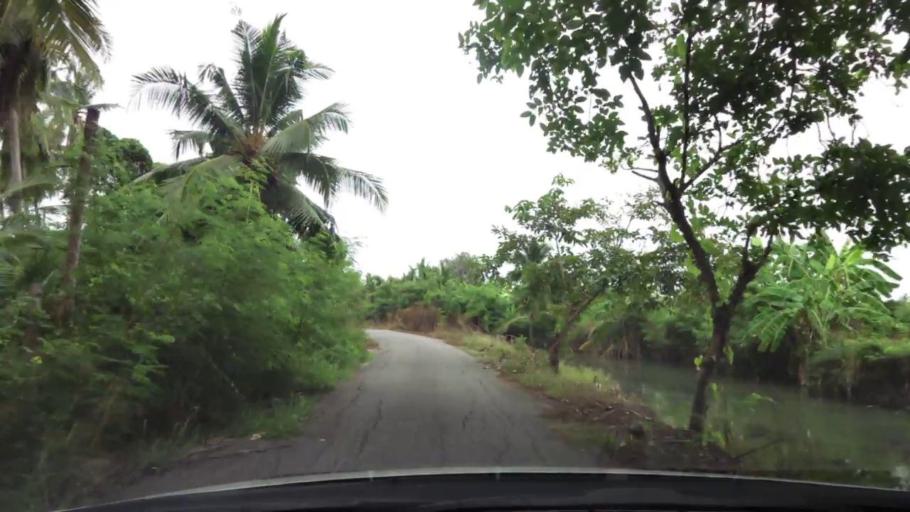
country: TH
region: Samut Sakhon
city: Ban Phaeo
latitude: 13.5937
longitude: 100.0307
